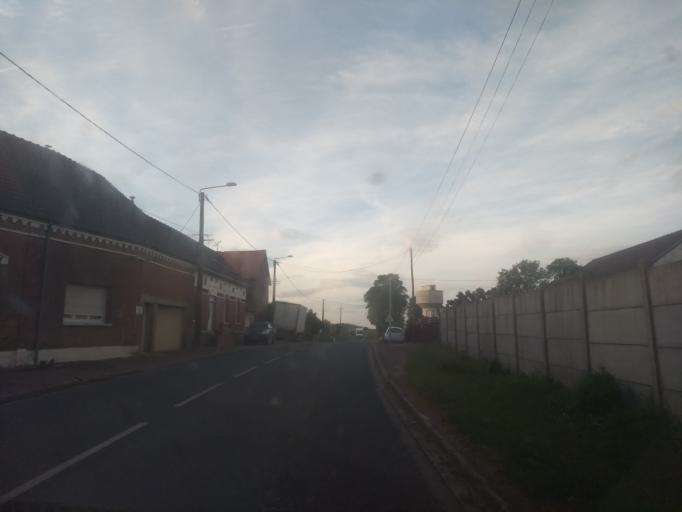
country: FR
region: Nord-Pas-de-Calais
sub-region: Departement du Pas-de-Calais
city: Bucquoy
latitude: 50.1209
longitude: 2.6926
